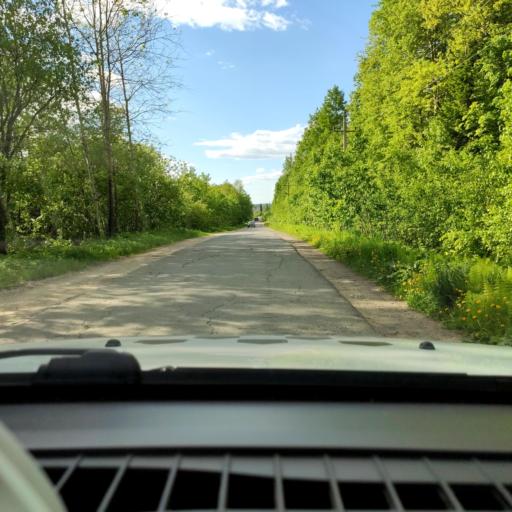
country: RU
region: Perm
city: Novyye Lyady
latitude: 58.0407
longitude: 56.6237
